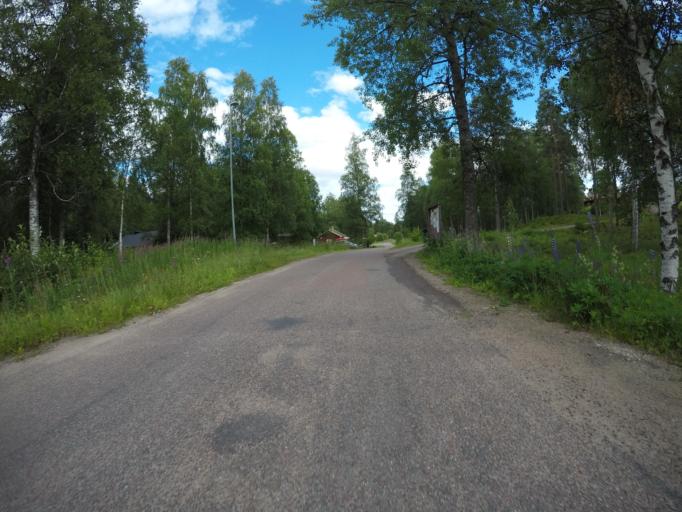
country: SE
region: OErebro
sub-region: Hallefors Kommun
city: Haellefors
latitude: 60.0427
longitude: 14.5154
